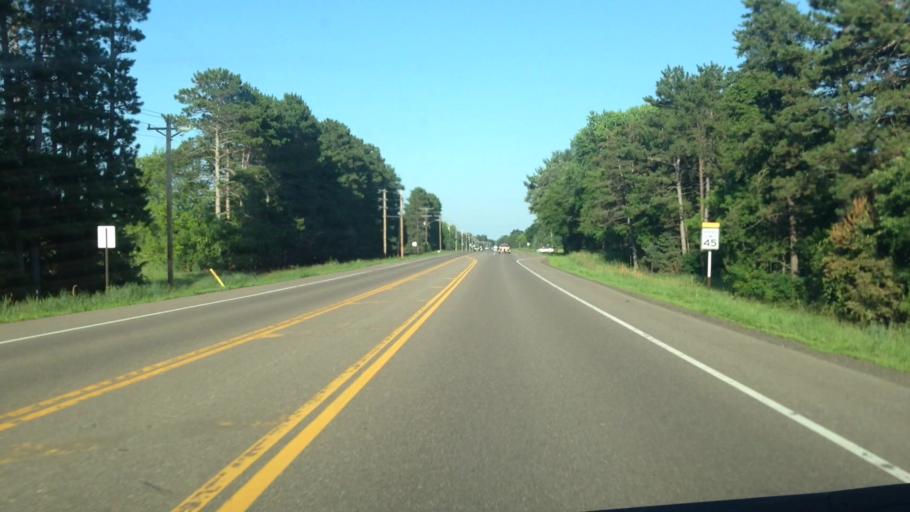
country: US
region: Minnesota
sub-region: Sherburne County
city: Zimmerman
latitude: 45.4437
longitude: -93.6172
